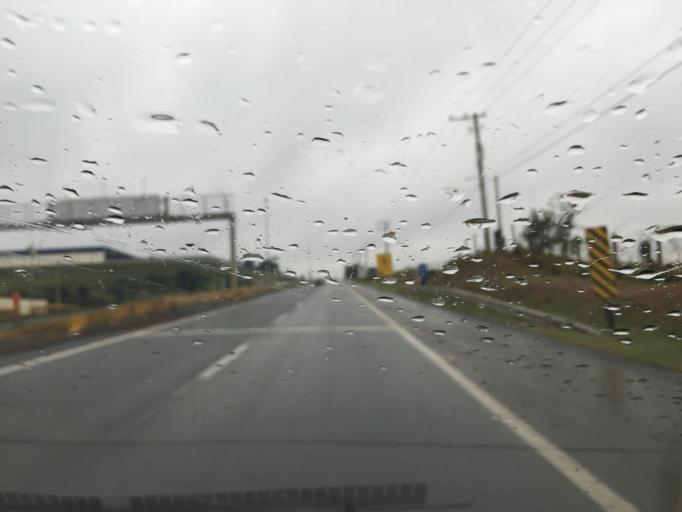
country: BR
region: Sao Paulo
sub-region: Itu
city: Itu
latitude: -23.2529
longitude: -47.3315
